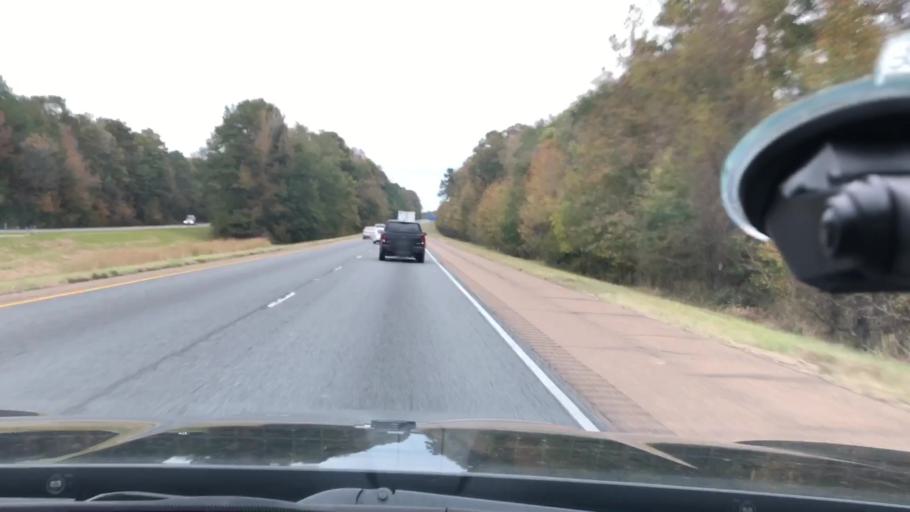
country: US
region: Arkansas
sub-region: Clark County
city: Gurdon
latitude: 33.9164
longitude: -93.2789
